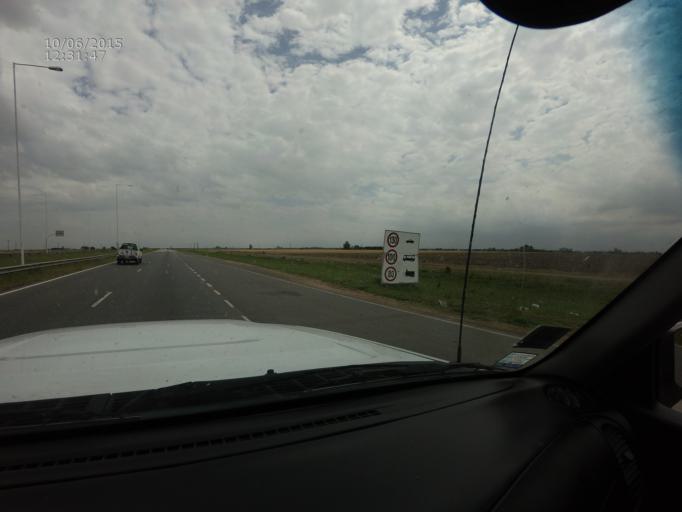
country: AR
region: Santa Fe
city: Carcarana
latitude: -32.8831
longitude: -61.1317
